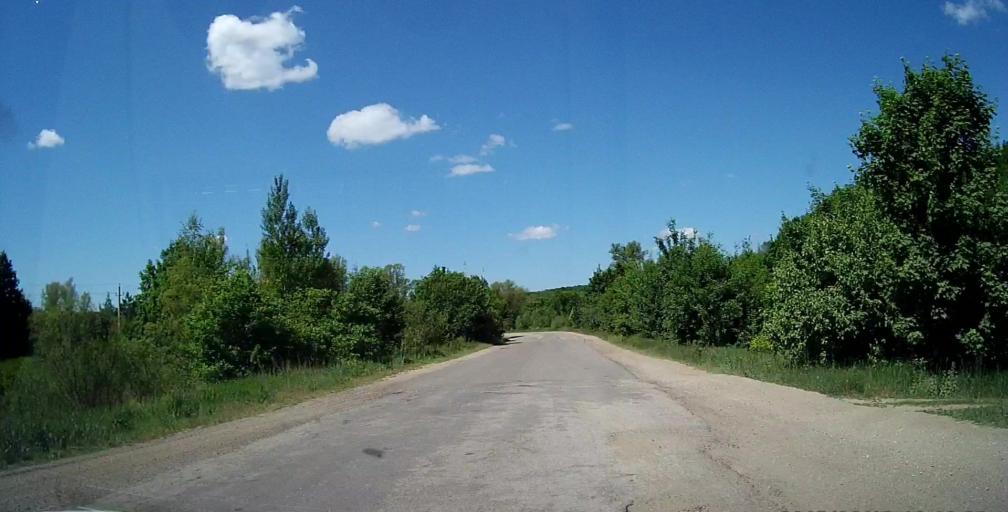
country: RU
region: Tula
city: Kurkino
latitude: 53.1973
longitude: 38.5538
